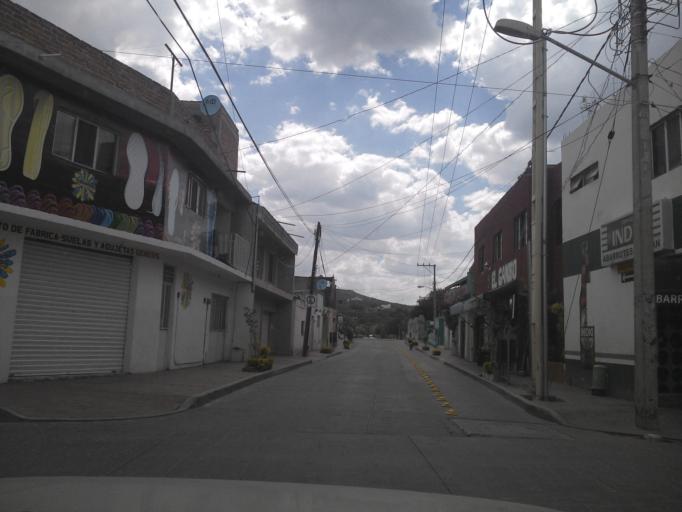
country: MX
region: Guanajuato
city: San Francisco del Rincon
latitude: 21.0304
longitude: -101.8822
